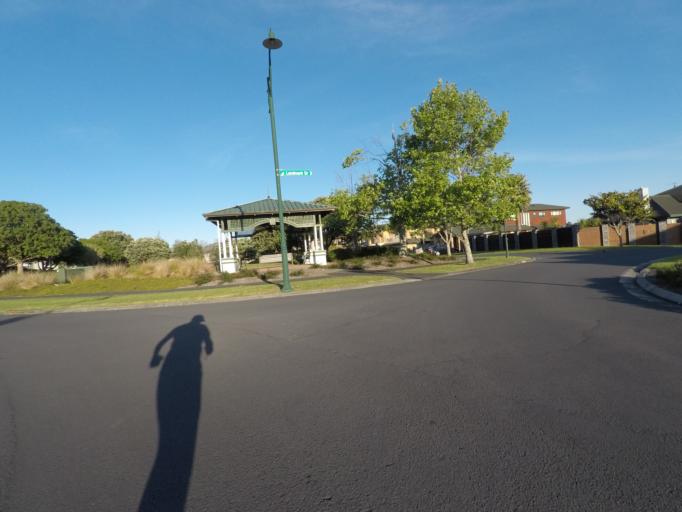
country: NZ
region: Auckland
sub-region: Auckland
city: Rosebank
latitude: -36.8470
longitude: 174.6523
